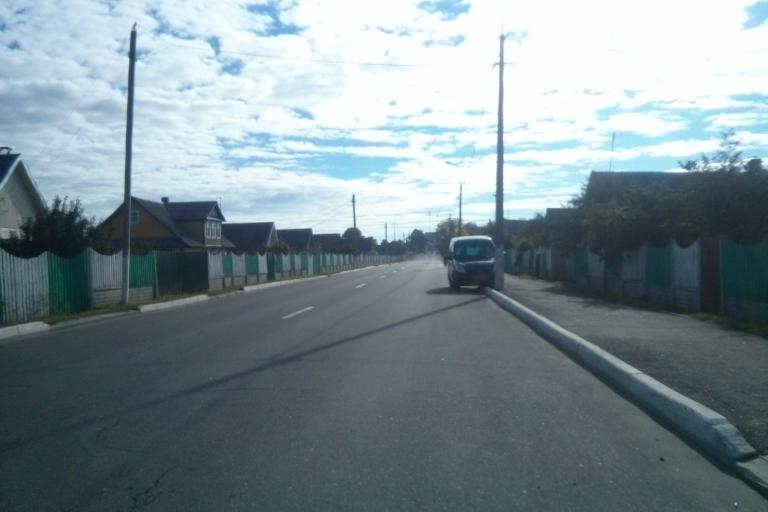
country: BY
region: Minsk
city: Chervyen'
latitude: 53.7170
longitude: 28.4083
